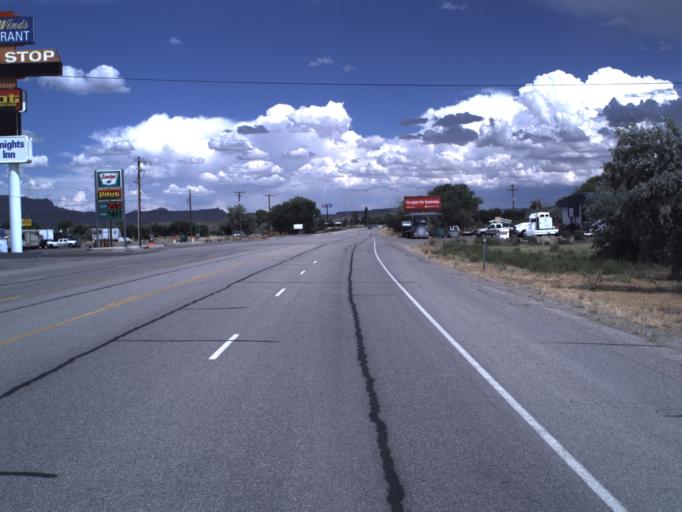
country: US
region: Utah
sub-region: Carbon County
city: East Carbon City
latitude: 38.9951
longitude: -110.1505
